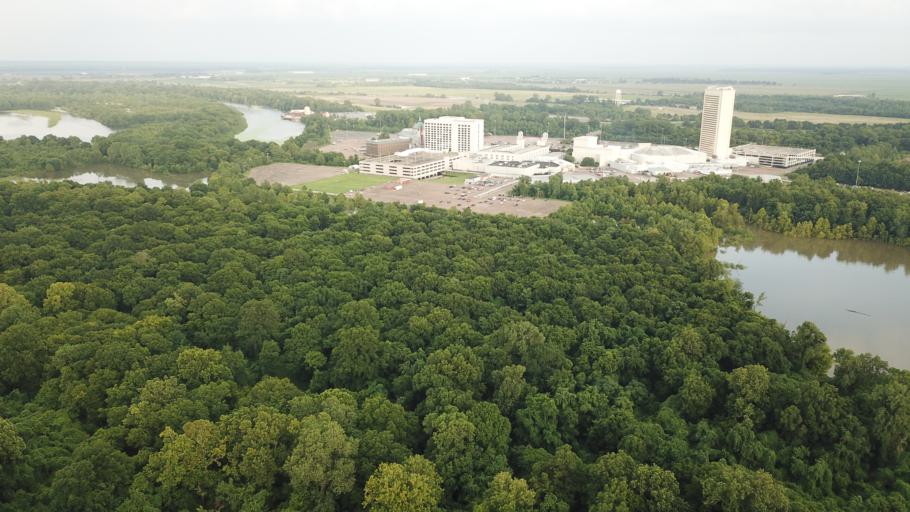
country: US
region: Mississippi
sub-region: Tunica County
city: North Tunica
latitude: 34.8537
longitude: -90.3373
